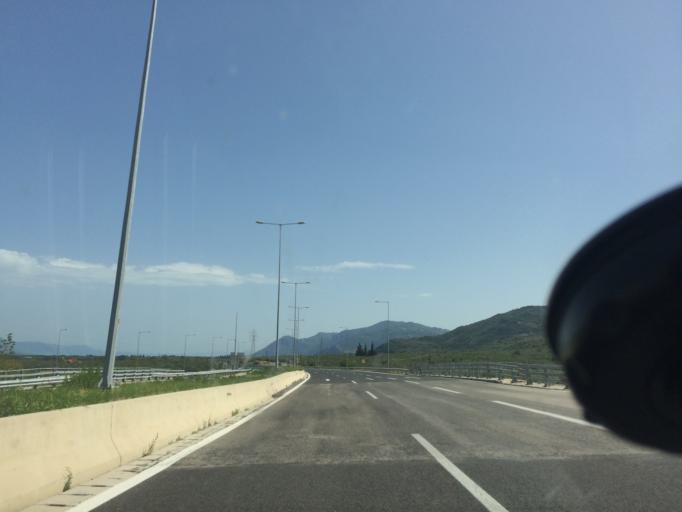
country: GR
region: Central Greece
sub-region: Nomos Fthiotidos
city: Molos
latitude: 38.8017
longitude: 22.6453
